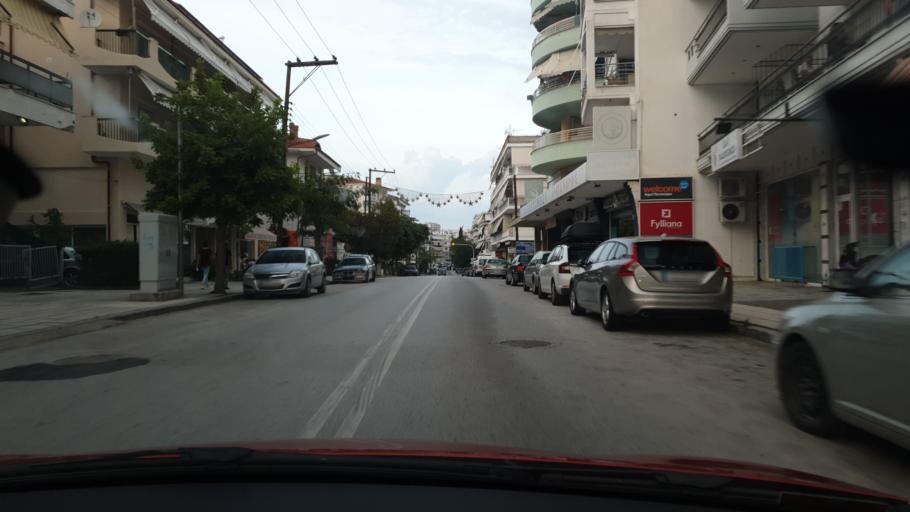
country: GR
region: Central Macedonia
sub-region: Nomos Kilkis
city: Kilkis
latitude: 40.9889
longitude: 22.8688
